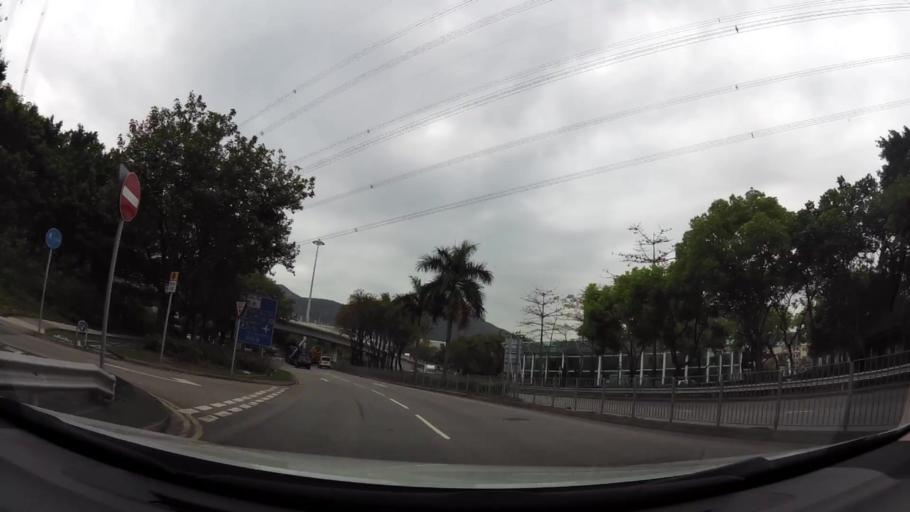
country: HK
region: Tuen Mun
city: Tuen Mun
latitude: 22.4153
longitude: 113.9822
